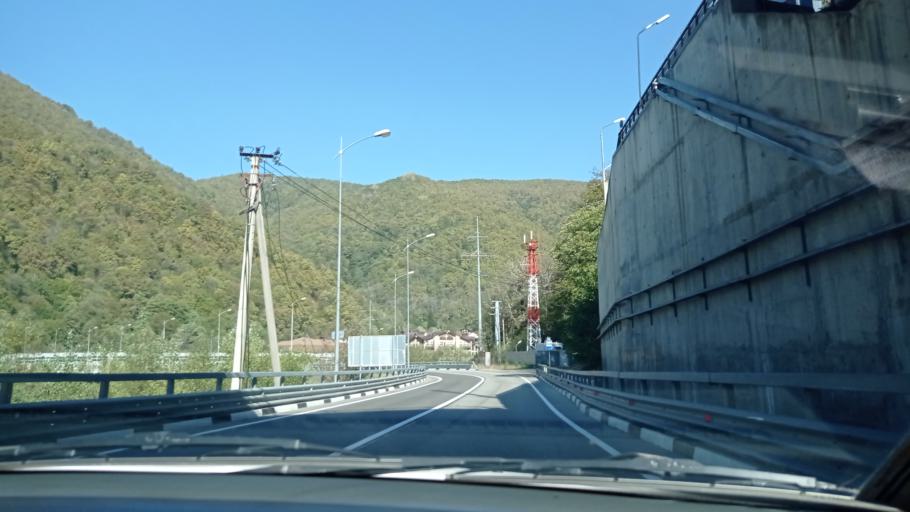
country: RU
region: Krasnodarskiy
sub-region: Sochi City
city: Krasnaya Polyana
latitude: 43.6843
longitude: 40.2457
